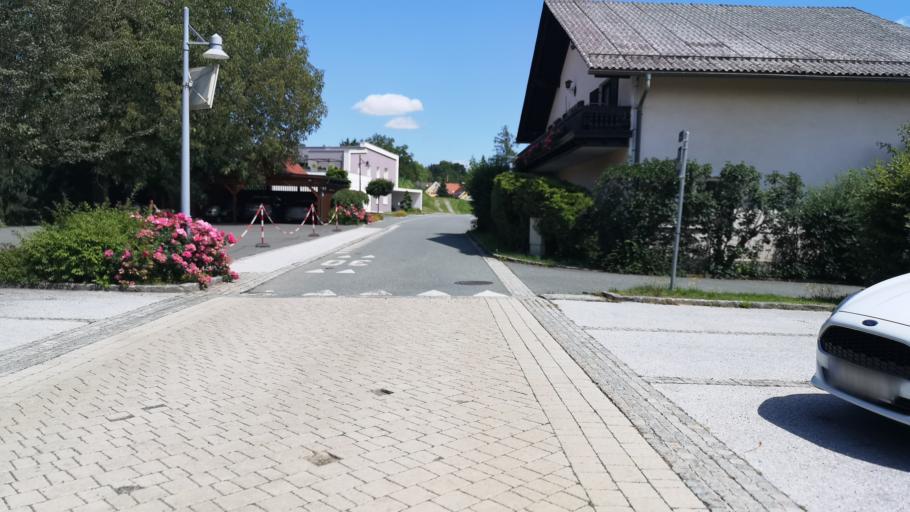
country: AT
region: Styria
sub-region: Politischer Bezirk Graz-Umgebung
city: Mellach
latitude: 46.9298
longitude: 15.5111
